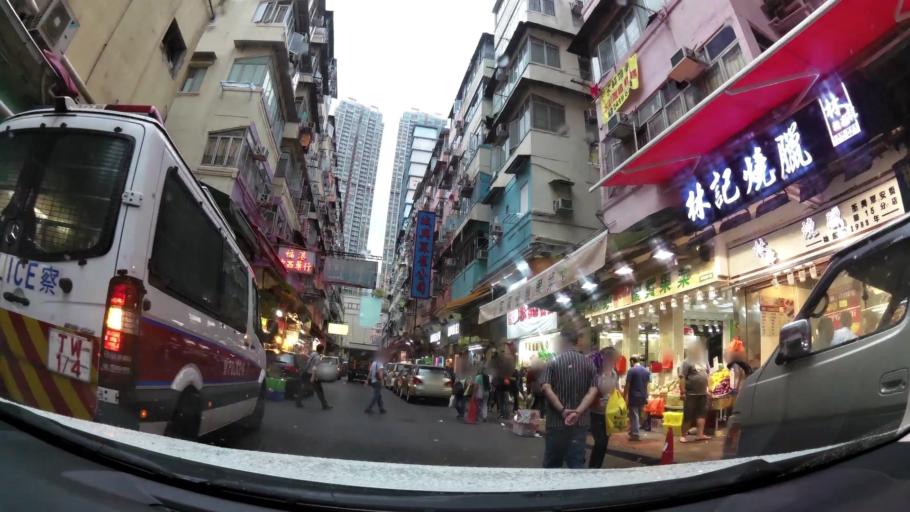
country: HK
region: Tsuen Wan
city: Tsuen Wan
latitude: 22.3685
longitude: 114.1159
